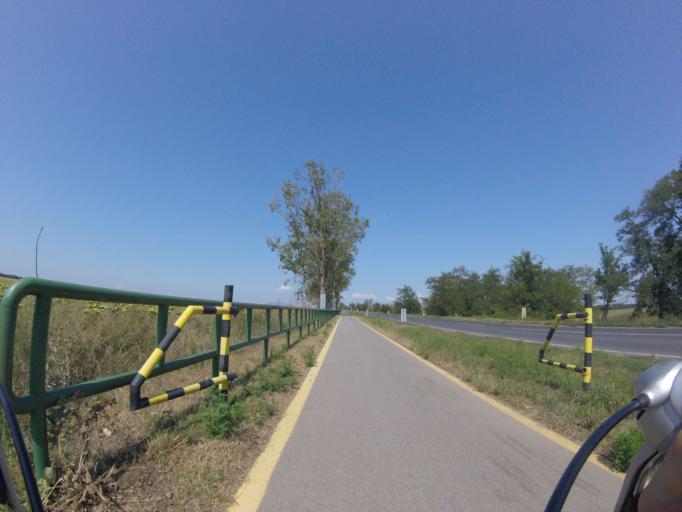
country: HU
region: Szabolcs-Szatmar-Bereg
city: Nyirtelek
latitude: 48.0171
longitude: 21.6206
